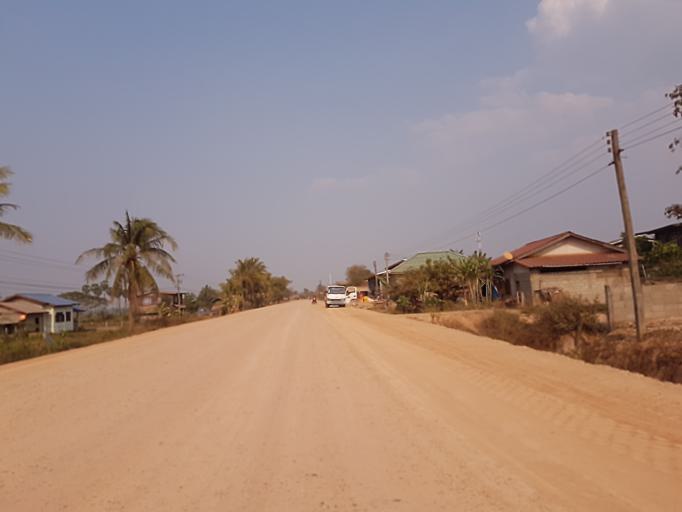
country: TH
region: Nong Khai
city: Nong Khai
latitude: 17.9826
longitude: 102.8886
